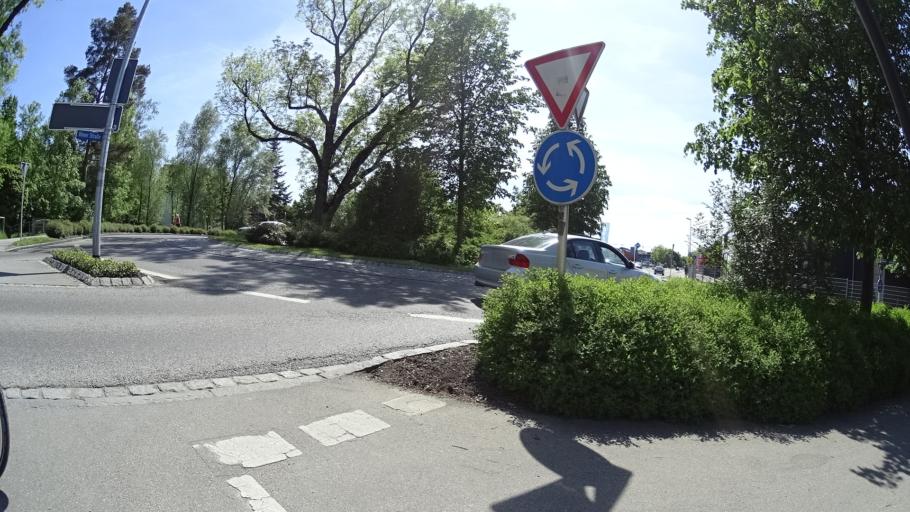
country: DE
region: Bavaria
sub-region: Swabia
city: Weissenhorn
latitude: 48.3081
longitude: 10.1548
